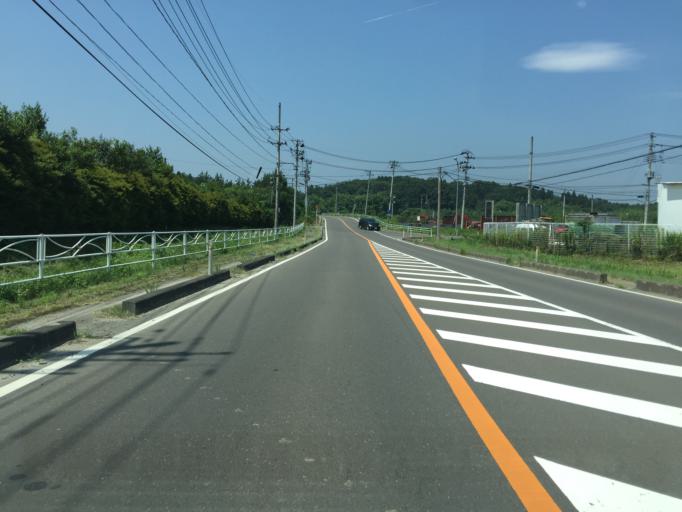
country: JP
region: Miyagi
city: Marumori
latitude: 37.9058
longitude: 140.7939
